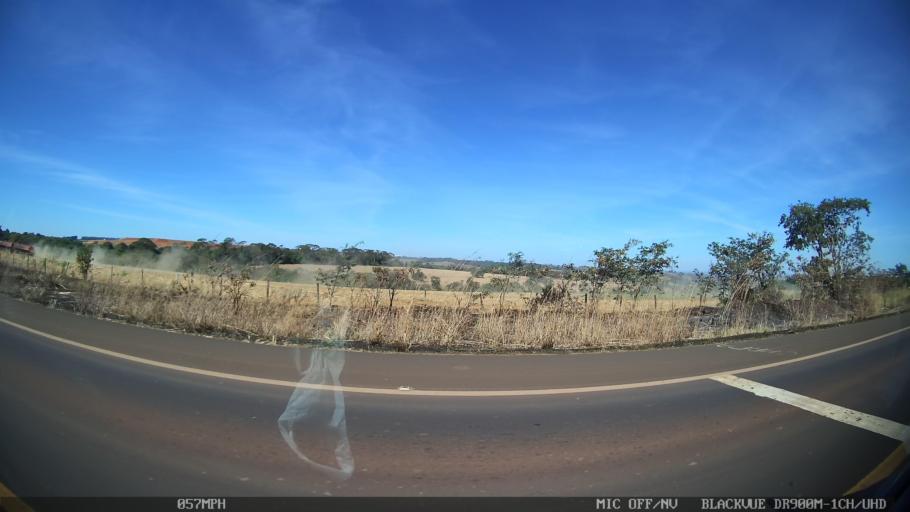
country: BR
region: Sao Paulo
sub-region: Franca
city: Franca
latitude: -20.5491
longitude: -47.4826
